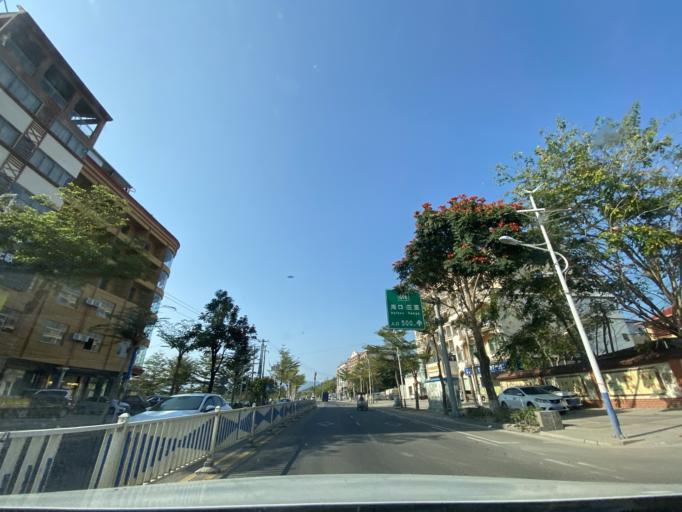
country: CN
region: Hainan
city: Yingzhou
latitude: 18.4302
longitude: 109.8536
